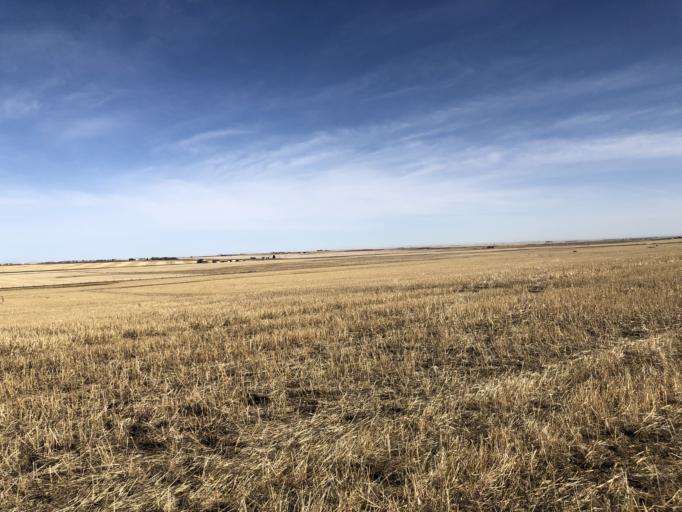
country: CA
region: Alberta
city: High River
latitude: 50.4747
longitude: -114.0117
